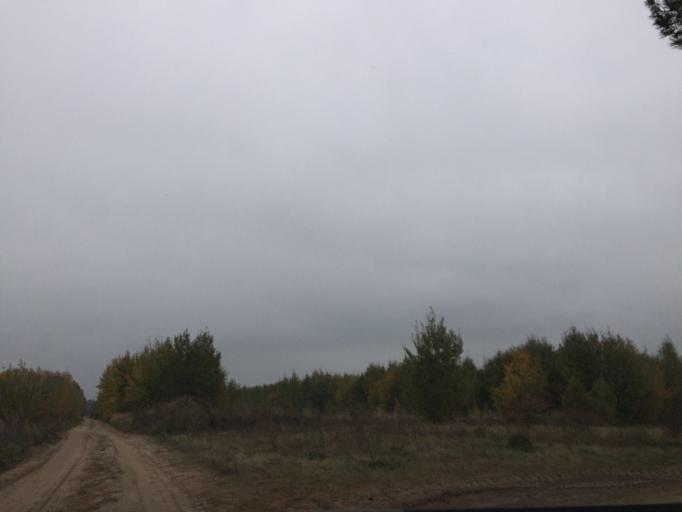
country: LV
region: Dobeles Rajons
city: Dobele
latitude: 56.6743
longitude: 23.4573
